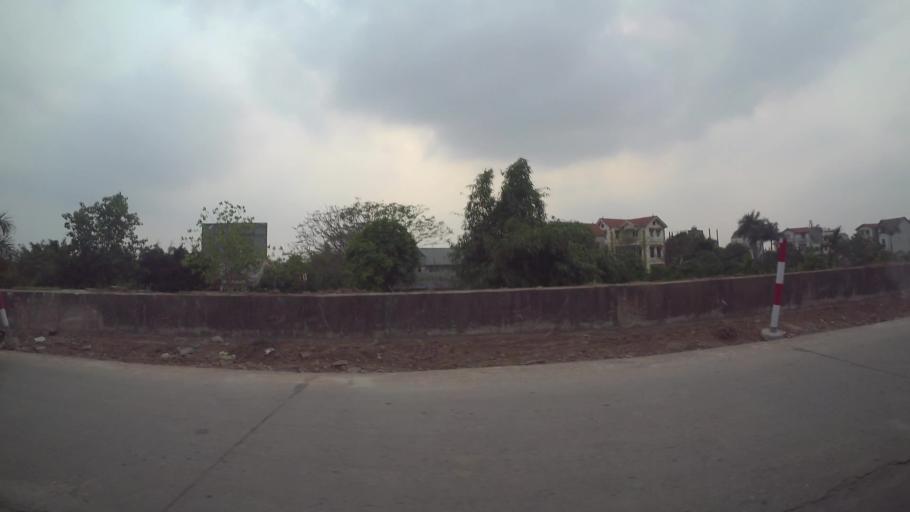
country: VN
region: Ha Noi
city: Trau Quy
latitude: 21.0085
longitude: 105.9052
